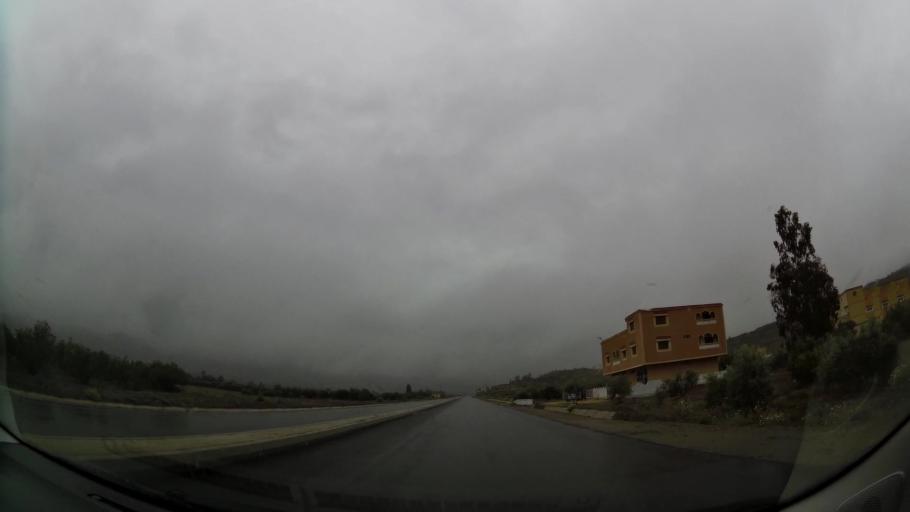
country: MA
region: Oriental
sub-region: Nador
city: Midar
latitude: 34.8350
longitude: -3.7201
